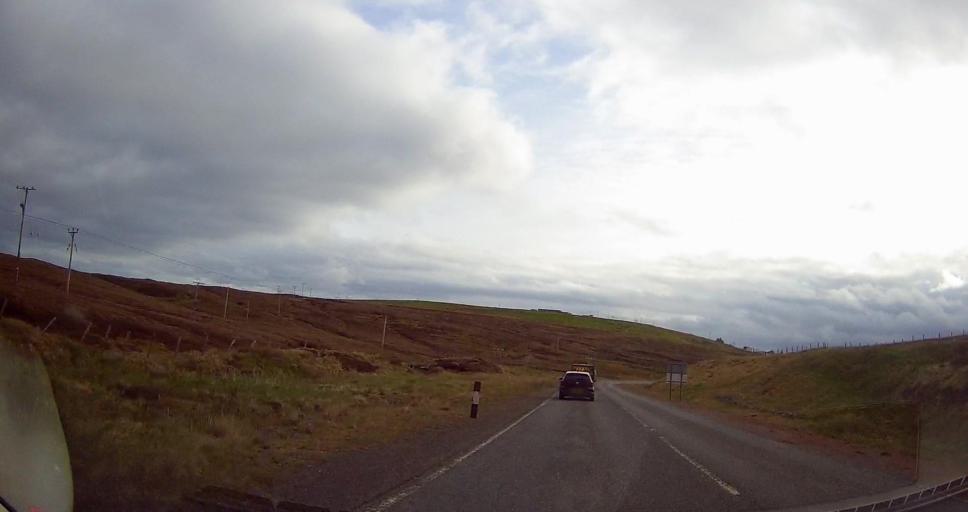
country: GB
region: Scotland
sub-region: Shetland Islands
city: Lerwick
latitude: 60.4433
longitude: -1.2162
